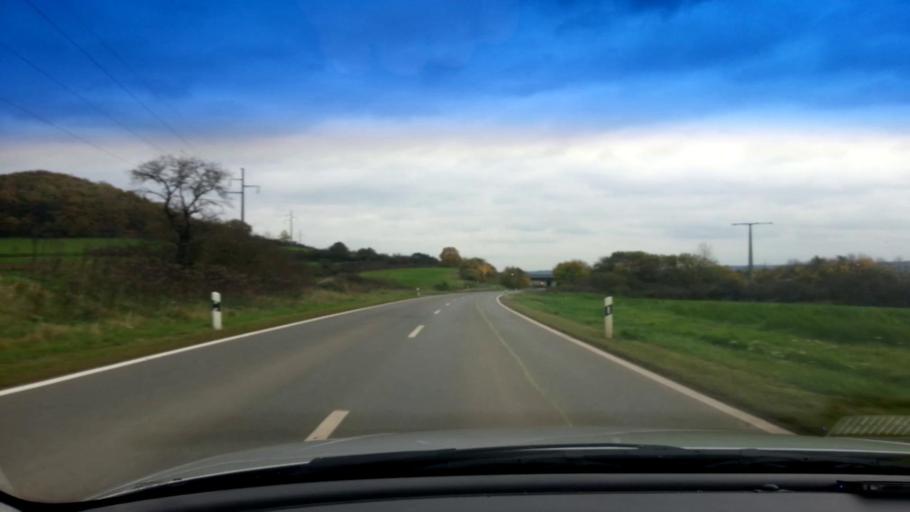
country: DE
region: Bavaria
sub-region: Regierungsbezirk Unterfranken
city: Stettfeld
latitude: 49.9640
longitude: 10.7290
